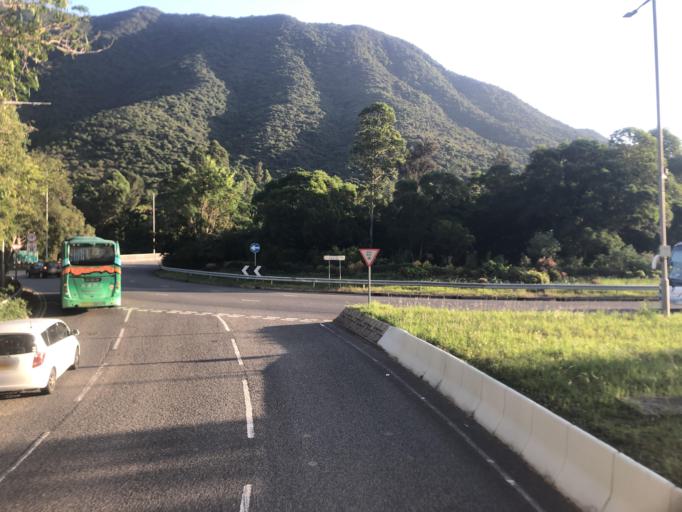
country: HK
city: Tai O
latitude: 22.2904
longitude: 113.9475
